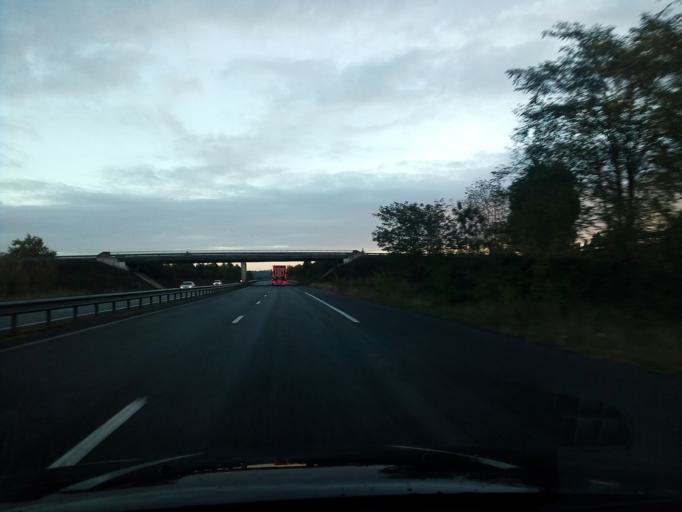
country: FR
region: Poitou-Charentes
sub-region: Departement de la Charente-Maritime
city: Montlieu-la-Garde
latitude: 45.2036
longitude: -0.3013
